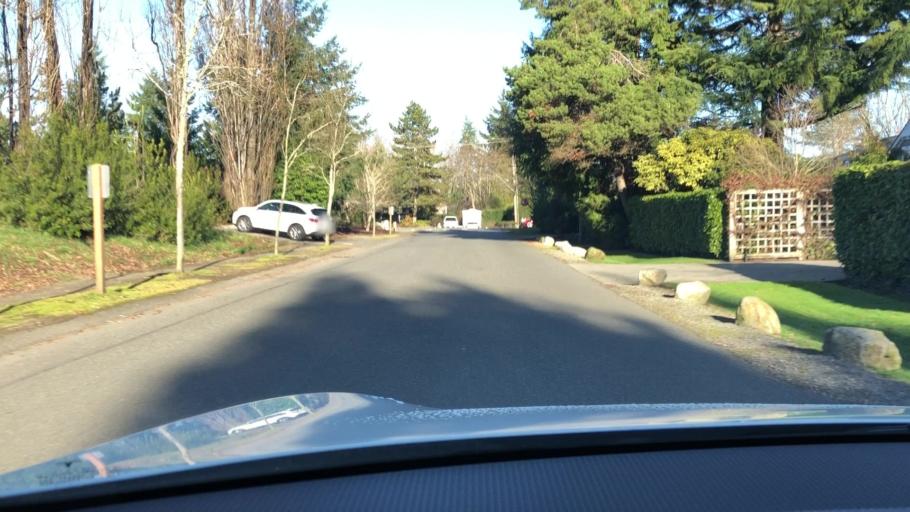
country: US
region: Washington
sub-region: King County
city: Medina
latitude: 47.6164
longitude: -122.2314
